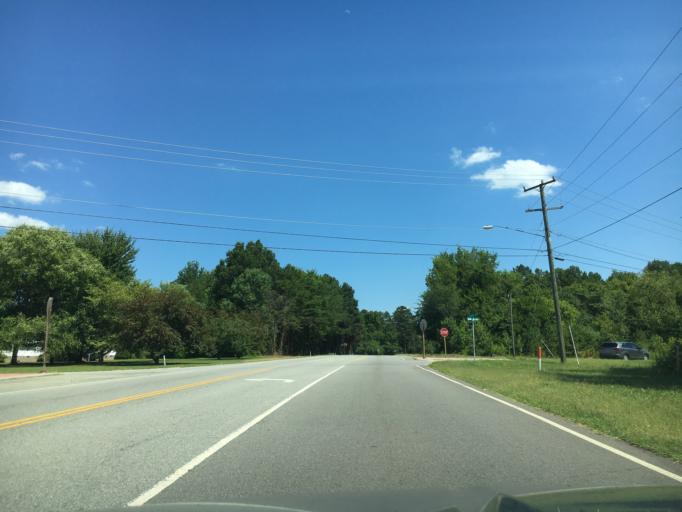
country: US
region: Virginia
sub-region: Halifax County
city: South Boston
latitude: 36.7137
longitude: -78.8889
